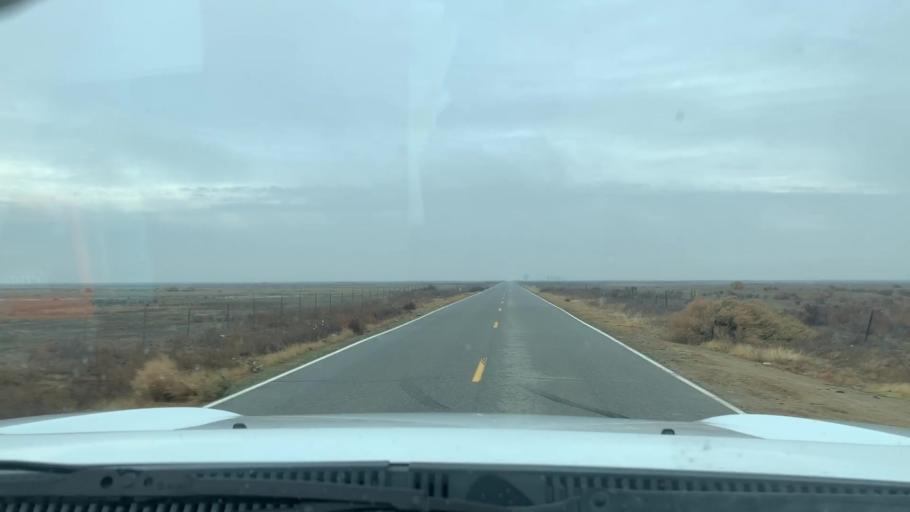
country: US
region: California
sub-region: Kern County
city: Lost Hills
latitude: 35.6453
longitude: -119.5801
